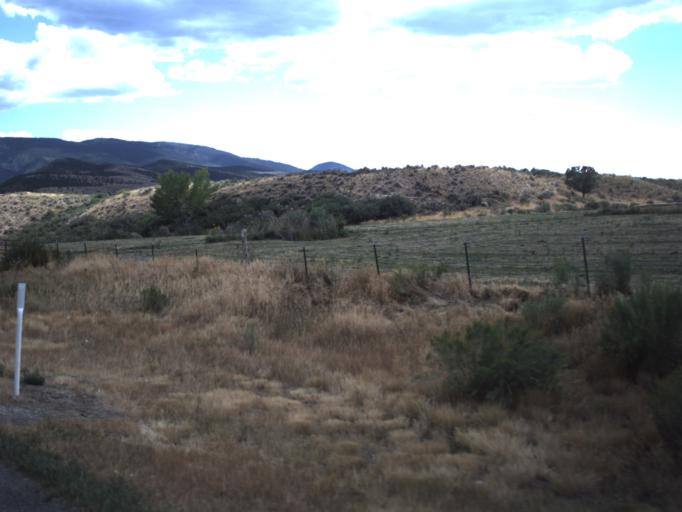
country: US
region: Utah
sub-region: Sanpete County
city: Centerfield
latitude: 39.1251
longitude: -111.7199
